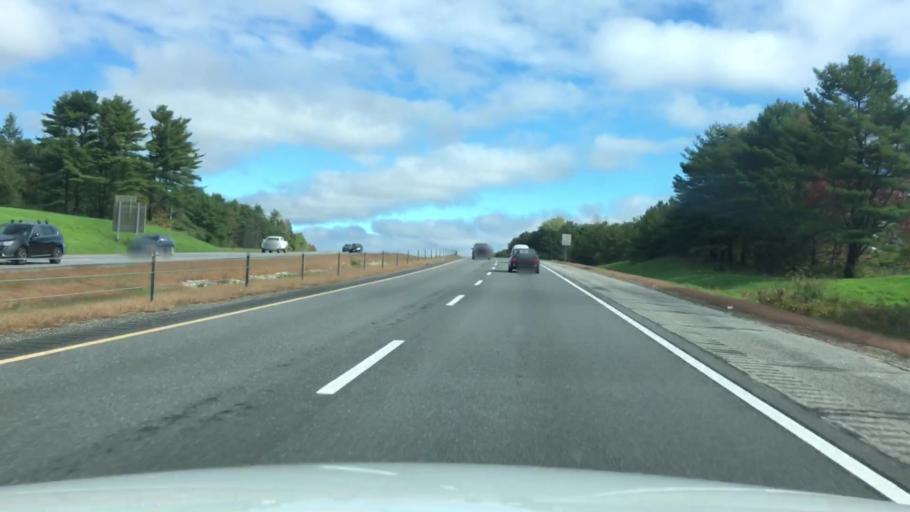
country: US
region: Maine
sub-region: Cumberland County
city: Yarmouth
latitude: 43.8148
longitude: -70.1501
